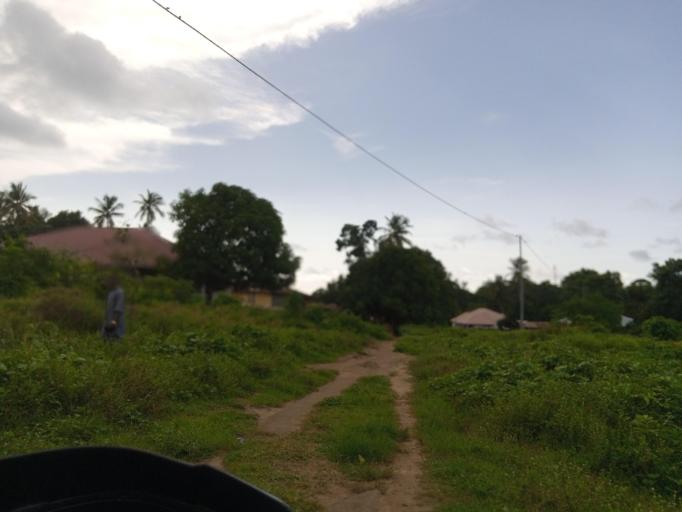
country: SL
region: Northern Province
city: Masoyila
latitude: 8.6021
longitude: -13.2032
